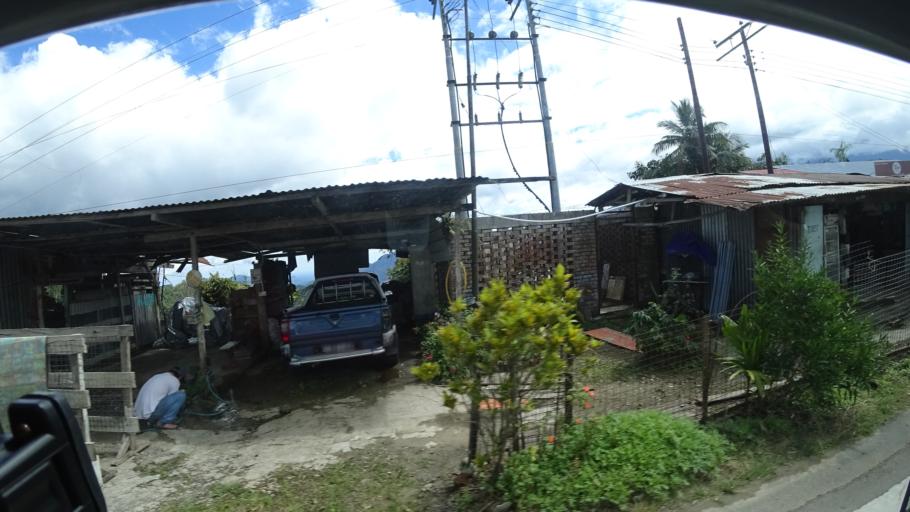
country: MY
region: Sabah
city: Ranau
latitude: 6.0284
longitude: 116.4617
